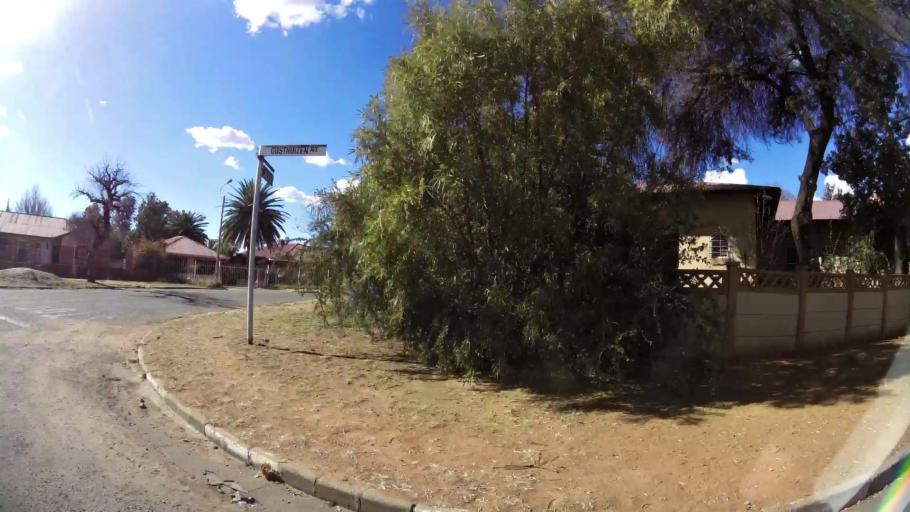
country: ZA
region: North-West
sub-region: Dr Kenneth Kaunda District Municipality
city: Klerksdorp
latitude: -26.8586
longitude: 26.6453
